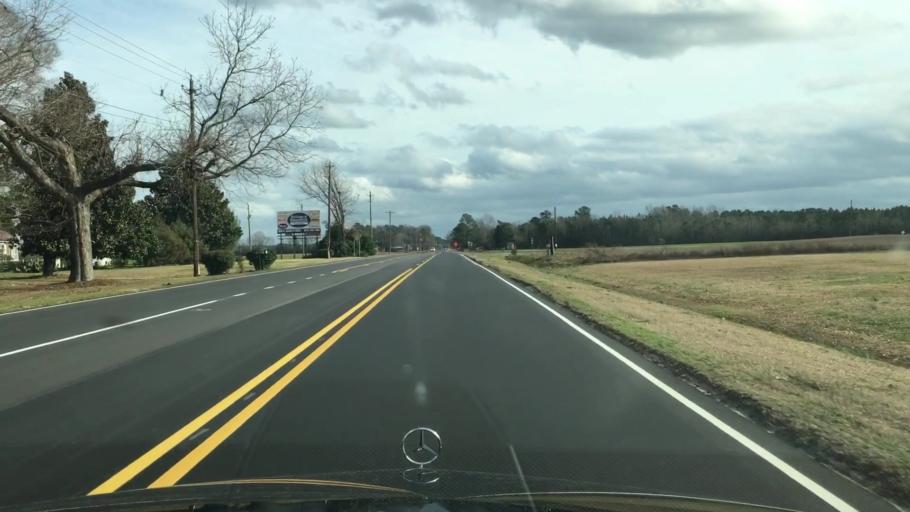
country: US
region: North Carolina
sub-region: Duplin County
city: Warsaw
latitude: 34.9845
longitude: -78.0409
